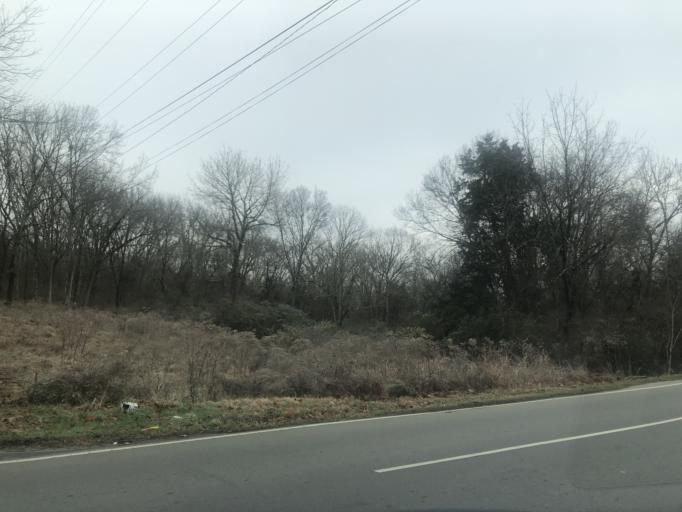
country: US
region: Tennessee
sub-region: Rutherford County
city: La Vergne
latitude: 36.0617
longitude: -86.6448
